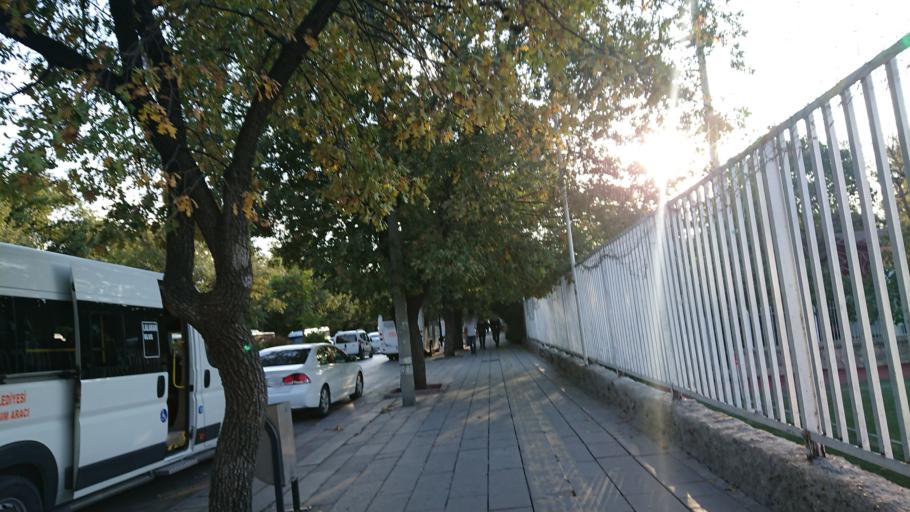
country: TR
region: Ankara
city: Ankara
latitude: 39.9389
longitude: 32.8478
